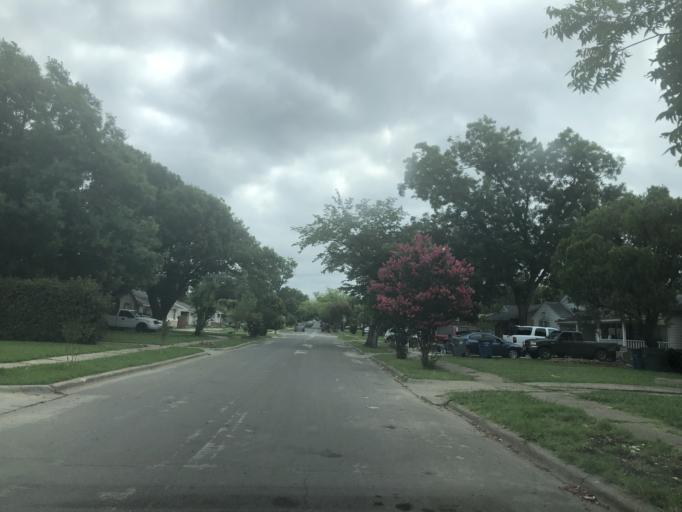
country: US
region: Texas
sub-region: Dallas County
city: University Park
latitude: 32.8672
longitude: -96.8540
